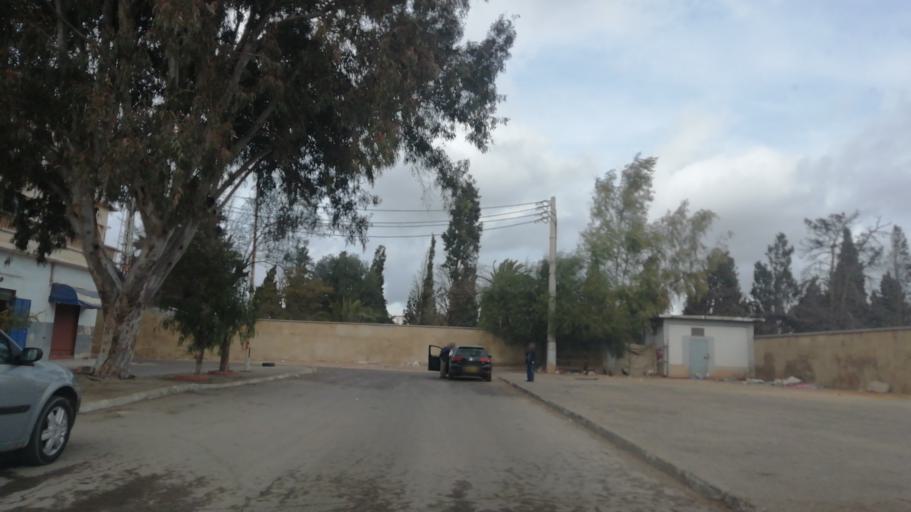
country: DZ
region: Oran
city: Oran
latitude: 35.6888
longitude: -0.6347
